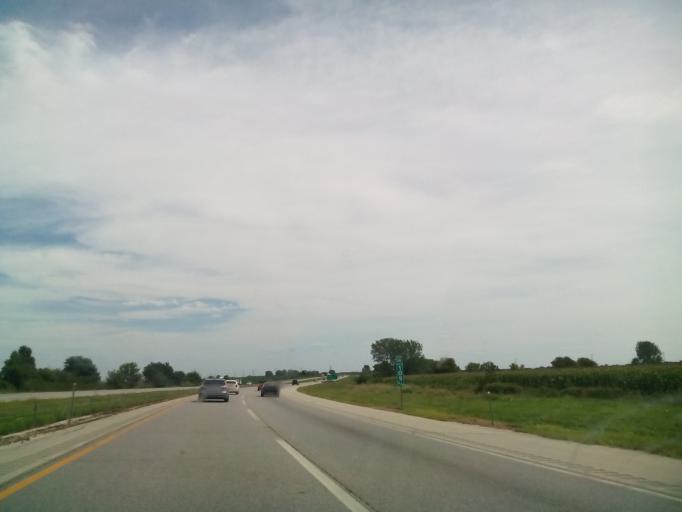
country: US
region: Illinois
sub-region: Kane County
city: Sugar Grove
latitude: 41.8174
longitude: -88.4586
